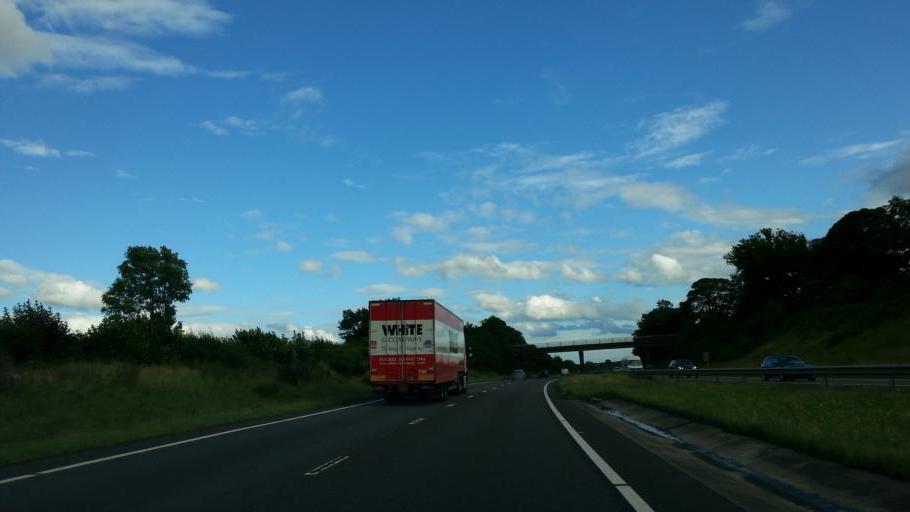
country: GB
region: England
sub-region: Nottinghamshire
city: Bircotes
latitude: 53.3852
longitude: -1.0585
